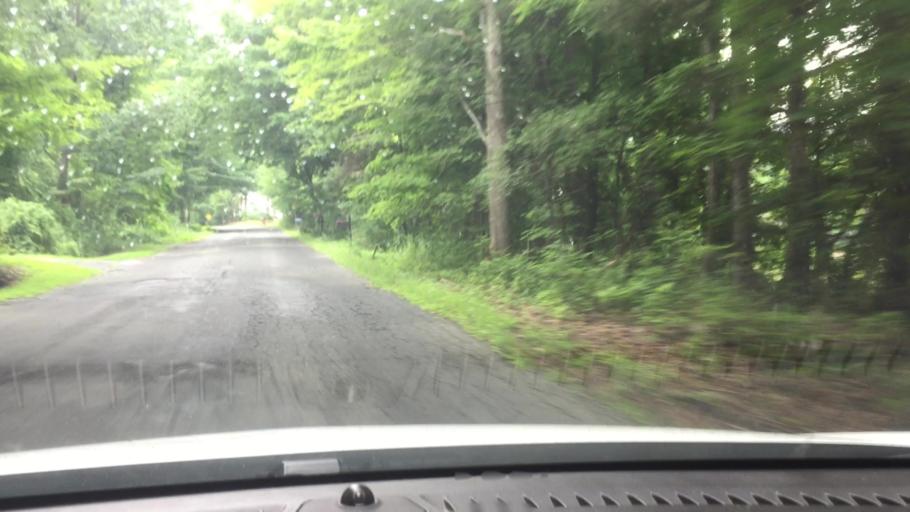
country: US
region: Massachusetts
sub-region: Berkshire County
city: Lee
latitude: 42.3011
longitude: -73.2801
